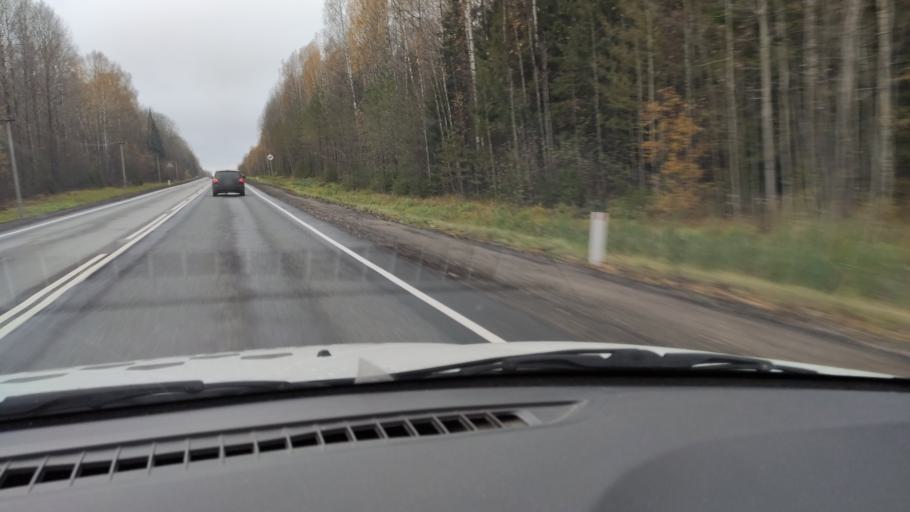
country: RU
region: Kirov
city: Belaya Kholunitsa
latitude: 58.9185
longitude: 51.1035
